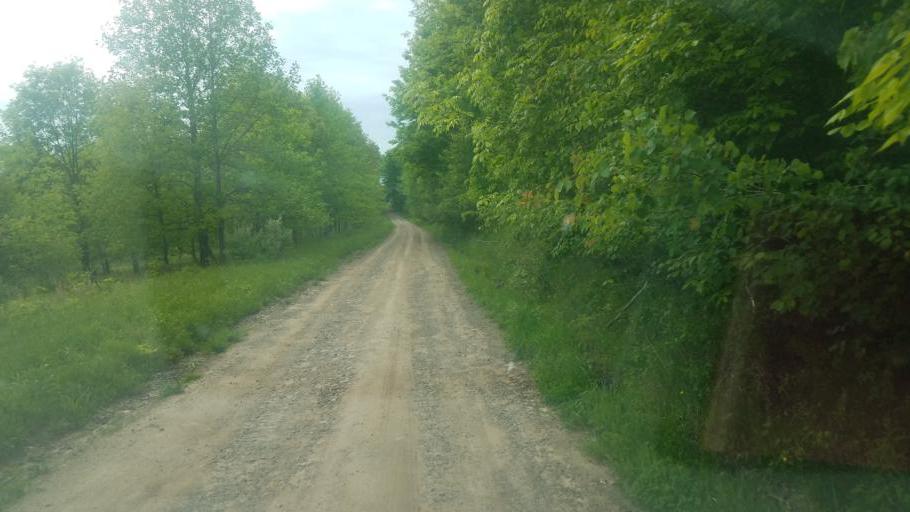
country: US
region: Pennsylvania
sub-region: Tioga County
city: Westfield
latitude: 41.9295
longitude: -77.6942
